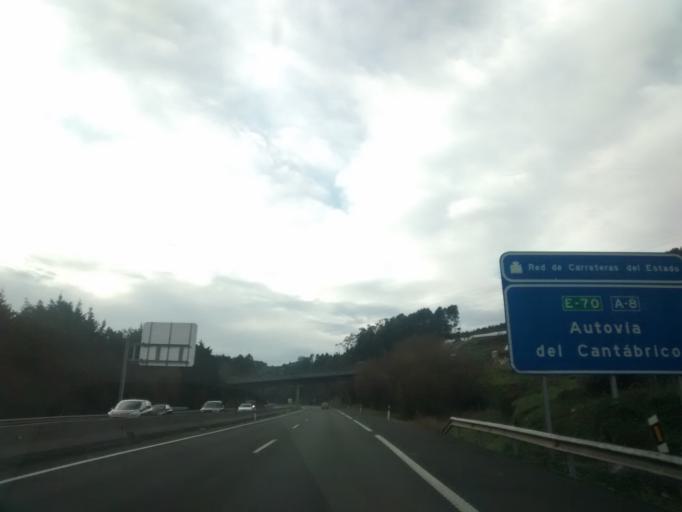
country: ES
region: Cantabria
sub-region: Provincia de Cantabria
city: Castro-Urdiales
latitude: 43.3860
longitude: -3.2333
